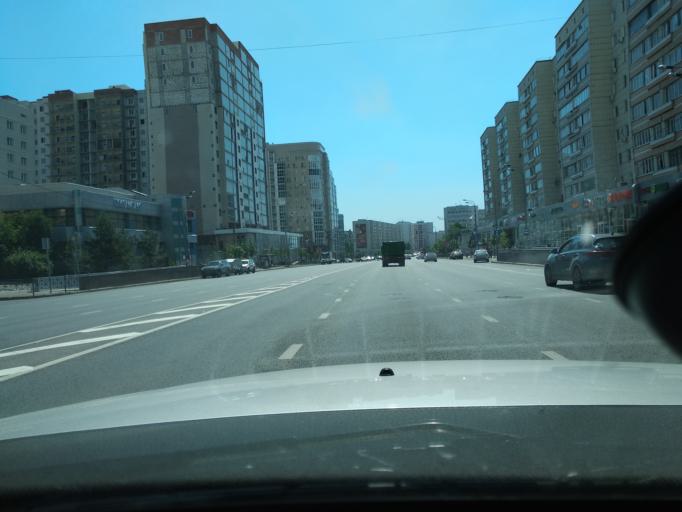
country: RU
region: Tatarstan
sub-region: Gorod Kazan'
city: Kazan
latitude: 55.7898
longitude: 49.1521
